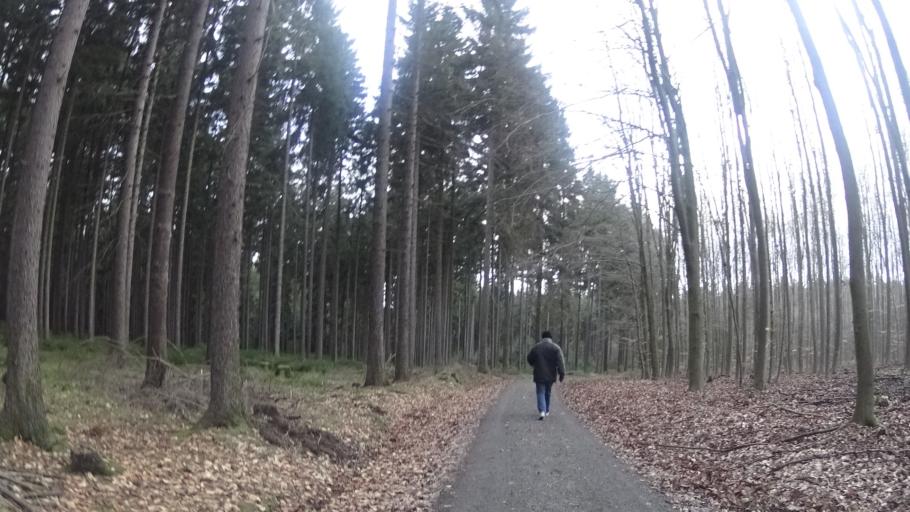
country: DE
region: Thuringia
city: Langenwolschendorf
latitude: 50.6162
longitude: 11.9847
